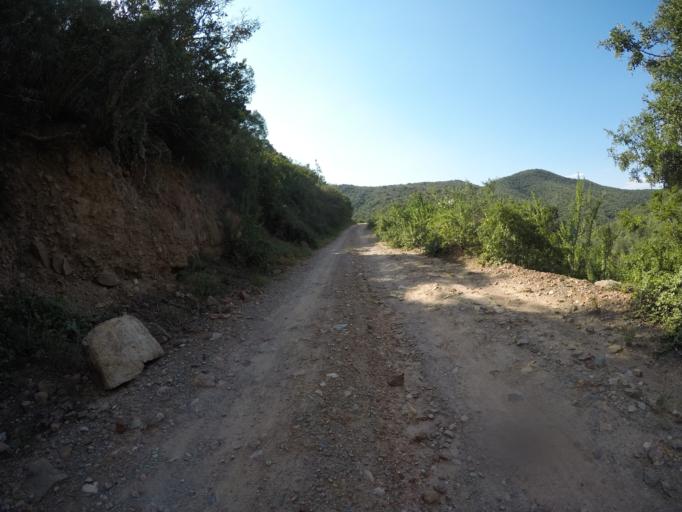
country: ZA
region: Eastern Cape
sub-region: Cacadu District Municipality
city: Kareedouw
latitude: -33.6538
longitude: 24.3482
